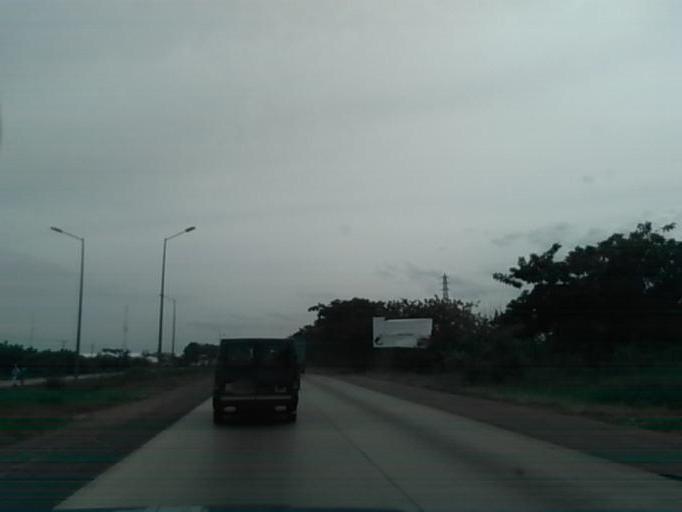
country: GH
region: Greater Accra
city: Medina Estates
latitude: 5.6403
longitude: -0.1301
